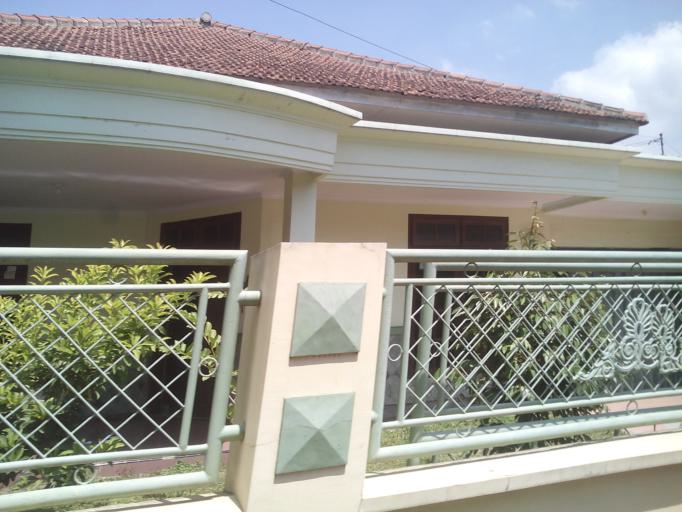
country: ID
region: East Java
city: Sumbersari Wetan
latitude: -8.1792
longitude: 113.7182
